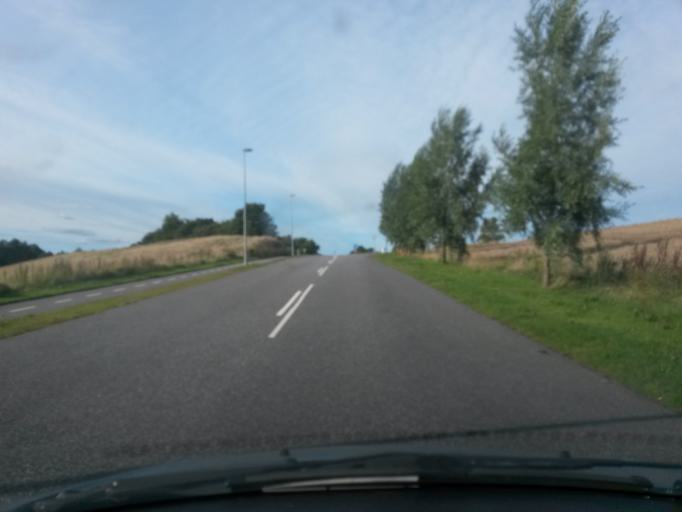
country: DK
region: Central Jutland
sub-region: Silkeborg Kommune
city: Kjellerup
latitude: 56.2959
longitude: 9.4274
